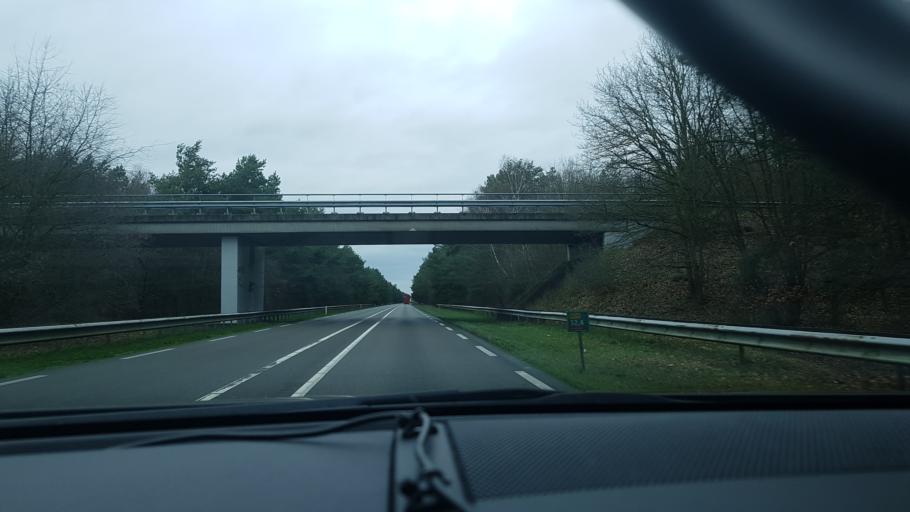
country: NL
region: North Brabant
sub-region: Gemeente Asten
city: Asten
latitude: 51.4431
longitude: 5.7308
